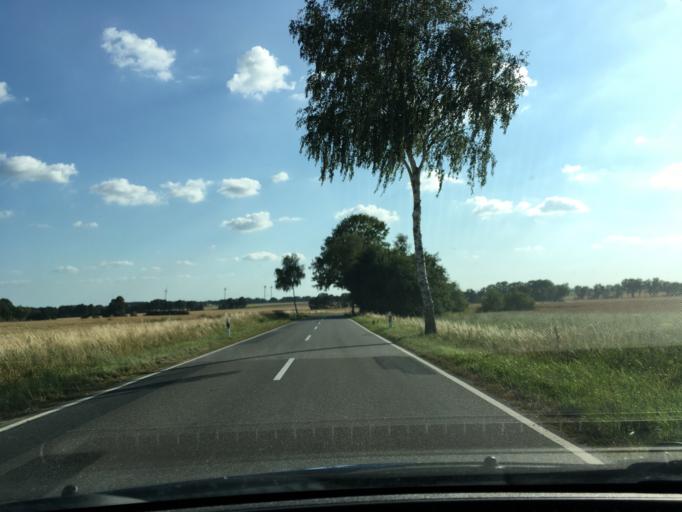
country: DE
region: Lower Saxony
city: Romstedt
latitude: 53.1459
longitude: 10.6592
